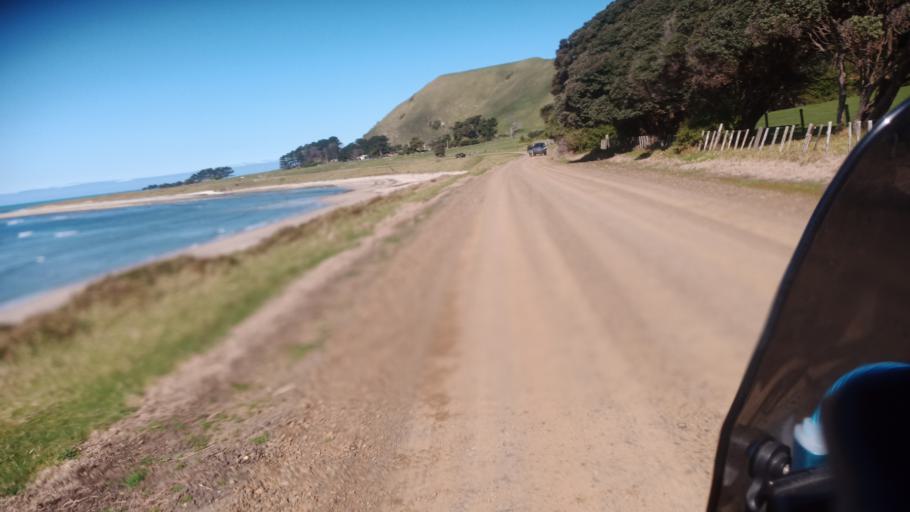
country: NZ
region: Gisborne
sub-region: Gisborne District
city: Gisborne
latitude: -39.0979
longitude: 177.9655
